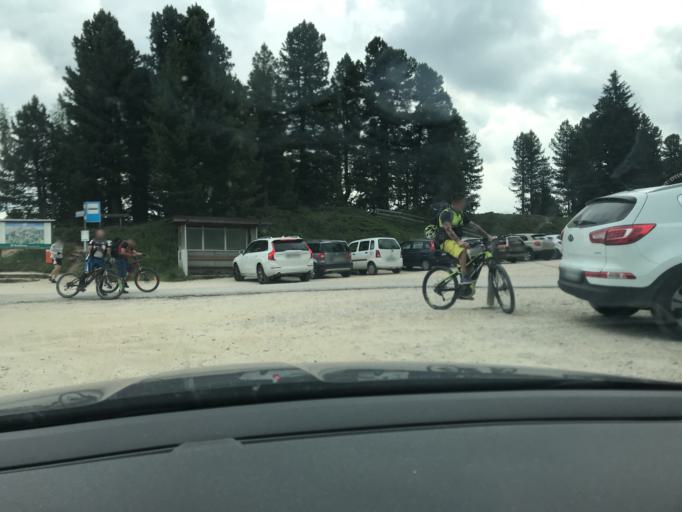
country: IT
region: Trentino-Alto Adige
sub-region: Bolzano
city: San Martino in Badia
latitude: 46.6749
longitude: 11.8143
